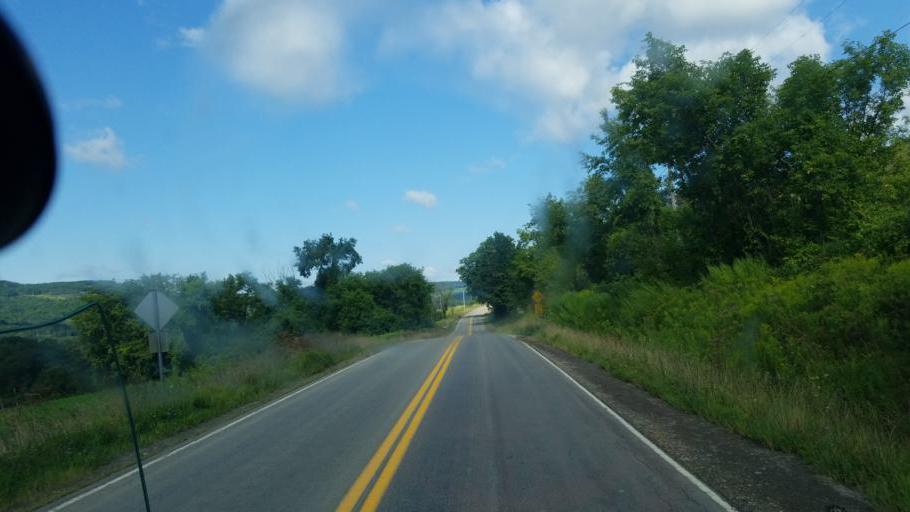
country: US
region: New York
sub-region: Steuben County
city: Hornell
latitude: 42.3014
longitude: -77.6323
